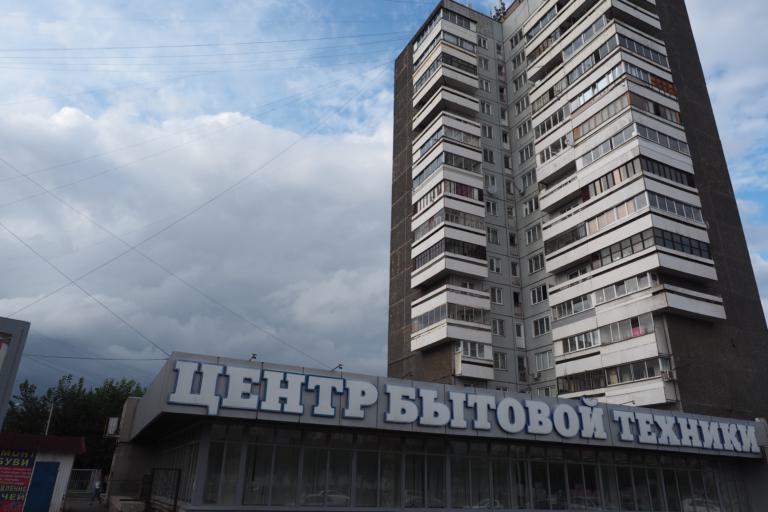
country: RU
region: Krasnoyarskiy
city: Krasnoyarsk
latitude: 56.0034
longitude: 92.9339
